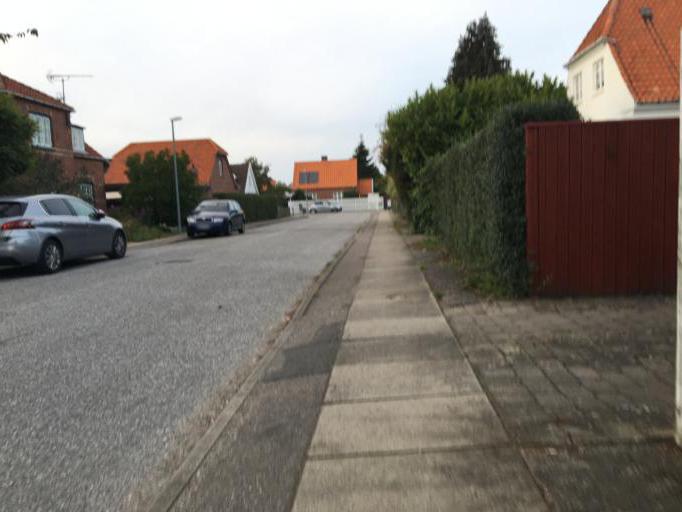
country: DK
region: Capital Region
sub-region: Tarnby Kommune
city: Tarnby
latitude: 55.6381
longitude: 12.6266
